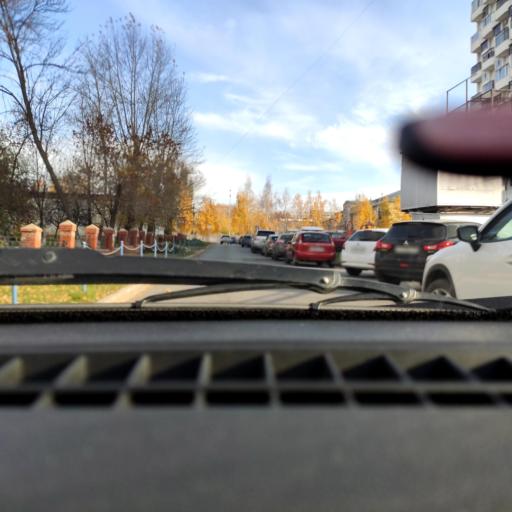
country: RU
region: Bashkortostan
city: Ufa
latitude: 54.7640
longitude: 56.0125
